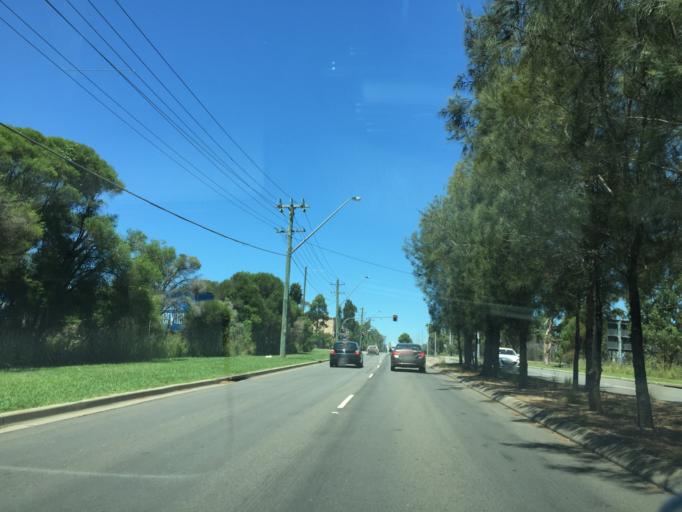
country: AU
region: New South Wales
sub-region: Blacktown
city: Doonside
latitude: -33.7862
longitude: 150.8722
